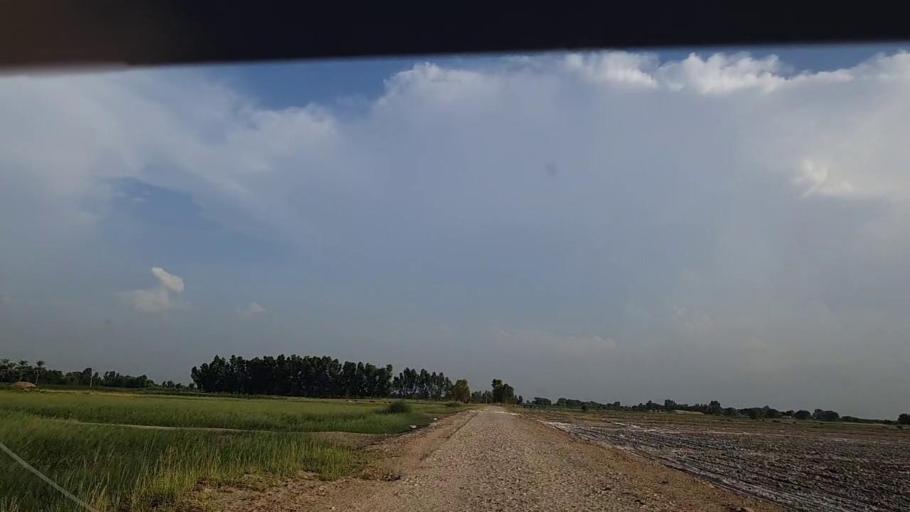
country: PK
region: Sindh
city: Khanpur
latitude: 27.8155
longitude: 69.3357
